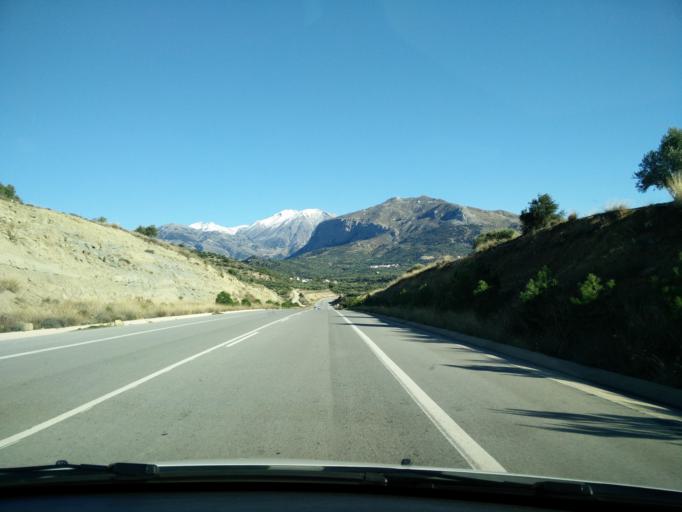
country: GR
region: Crete
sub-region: Nomos Irakleiou
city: Arkalochori
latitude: 35.0802
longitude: 25.3229
